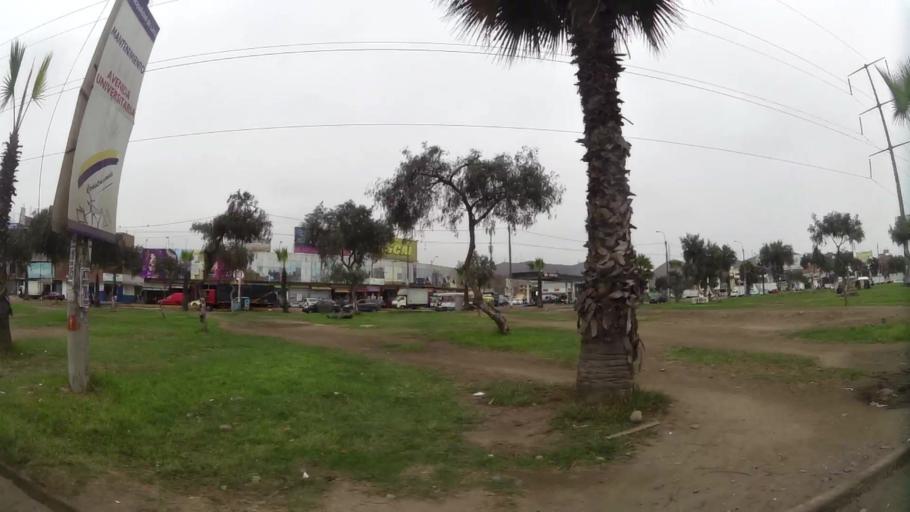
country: PE
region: Lima
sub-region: Lima
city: Independencia
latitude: -11.9900
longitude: -77.0819
